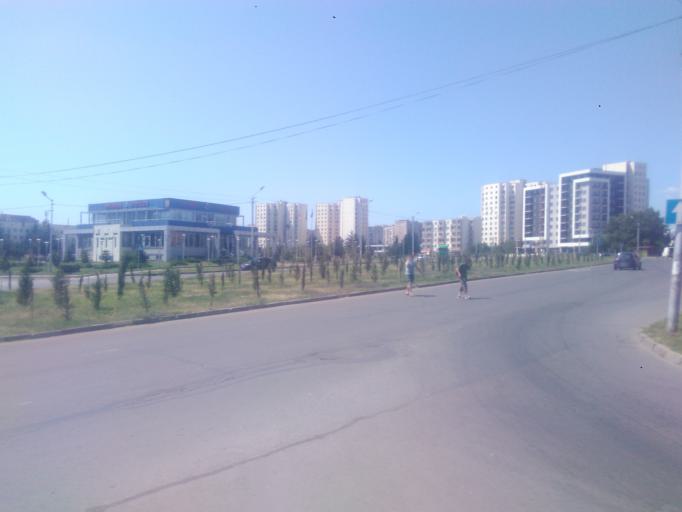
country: GE
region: T'bilisi
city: Tbilisi
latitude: 41.7054
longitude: 44.8835
